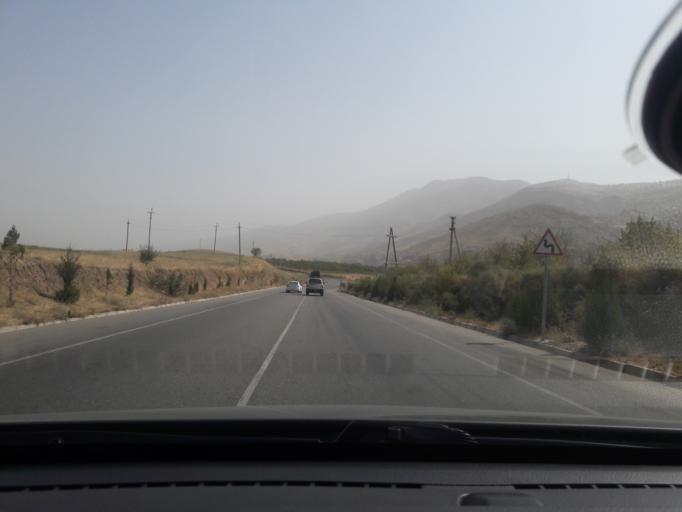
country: TJ
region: Republican Subordination
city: Vahdat
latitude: 38.4878
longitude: 69.1657
